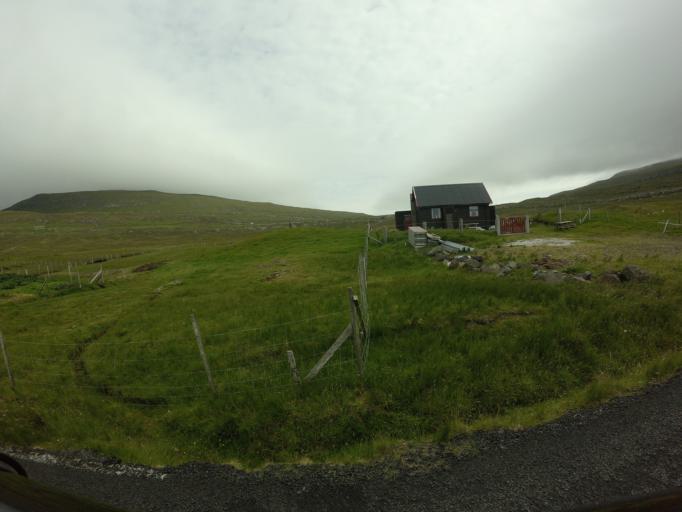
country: FO
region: Sandoy
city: Sandur
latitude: 61.8196
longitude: -6.7495
